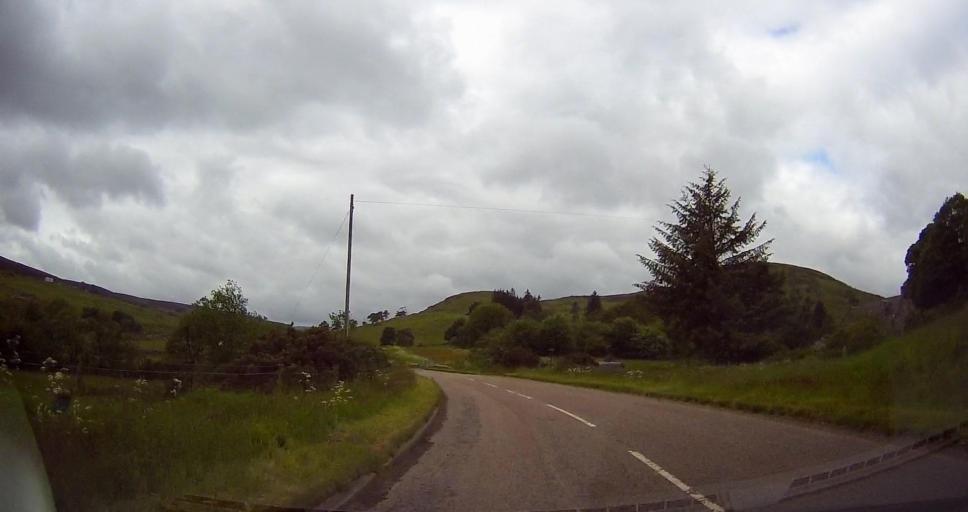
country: GB
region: Scotland
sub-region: Highland
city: Dornoch
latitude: 58.0069
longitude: -4.2072
